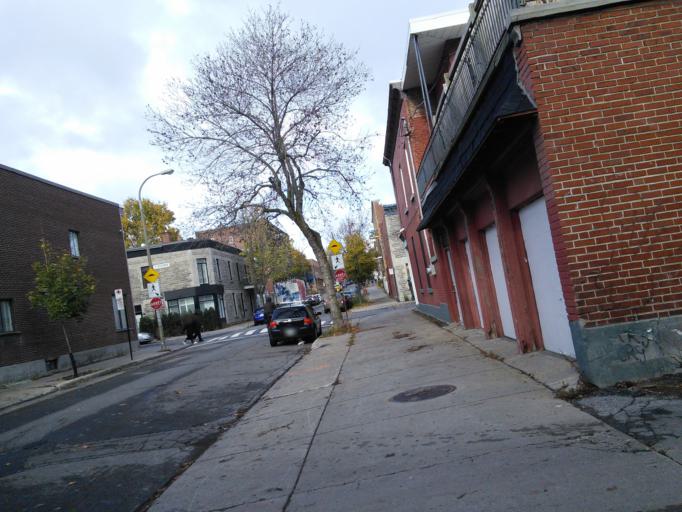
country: CA
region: Quebec
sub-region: Montreal
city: Montreal
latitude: 45.5280
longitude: -73.5842
